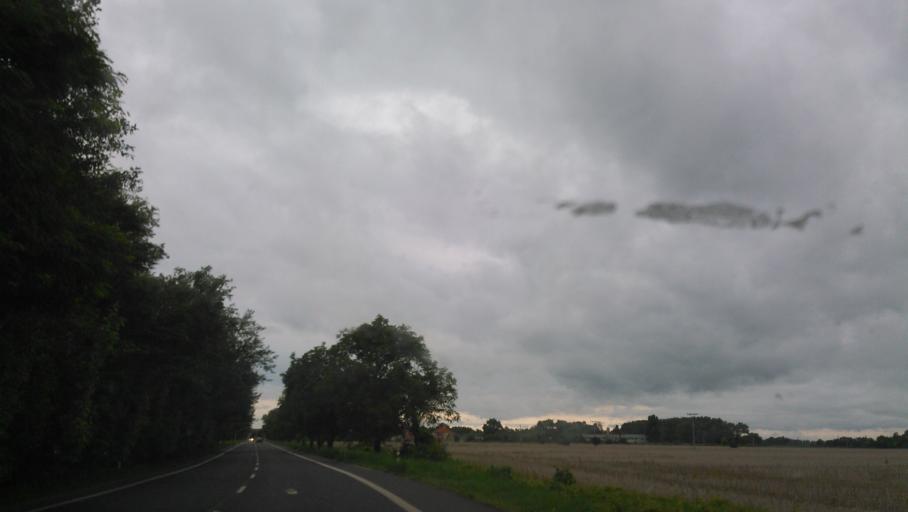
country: SK
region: Trnavsky
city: Dunajska Streda
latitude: 47.9618
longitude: 17.6945
